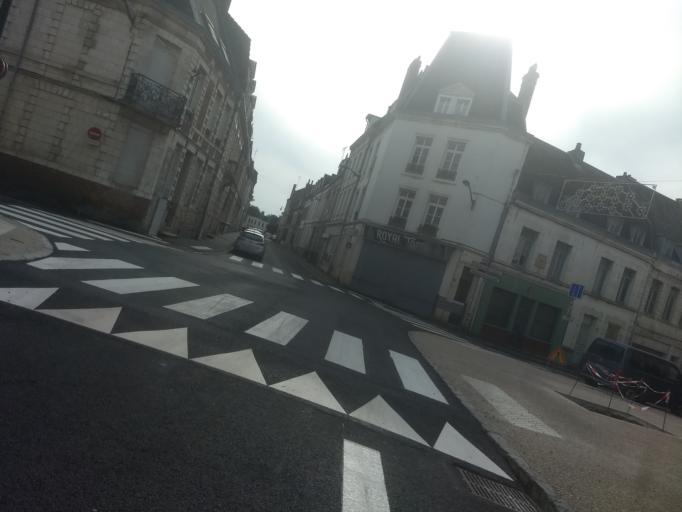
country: FR
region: Nord-Pas-de-Calais
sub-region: Departement du Pas-de-Calais
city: Arras
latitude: 50.2922
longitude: 2.7678
